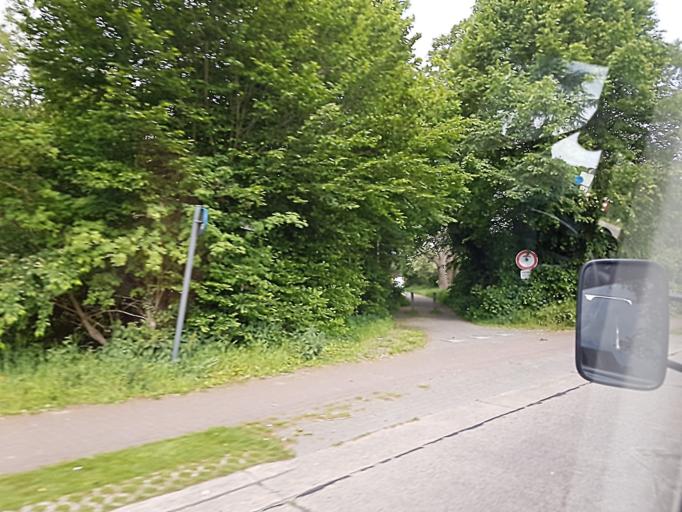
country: BE
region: Flanders
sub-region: Provincie Limburg
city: Bocholt
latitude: 51.1904
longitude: 5.5150
